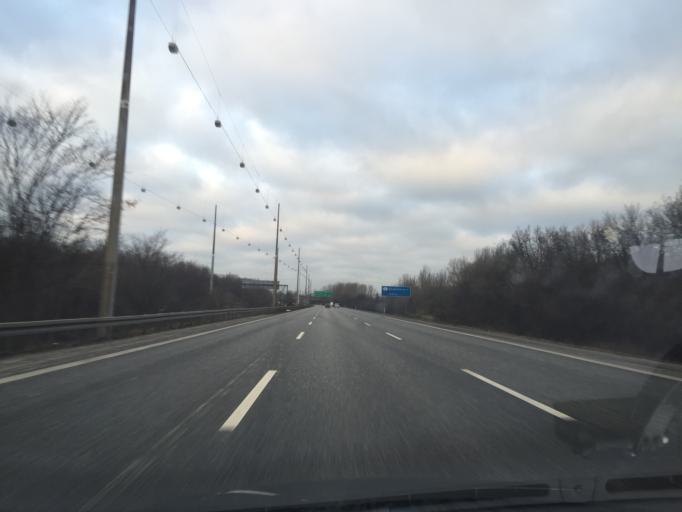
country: DK
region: Capital Region
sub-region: Albertslund Kommune
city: Albertslund
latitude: 55.6489
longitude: 12.3304
